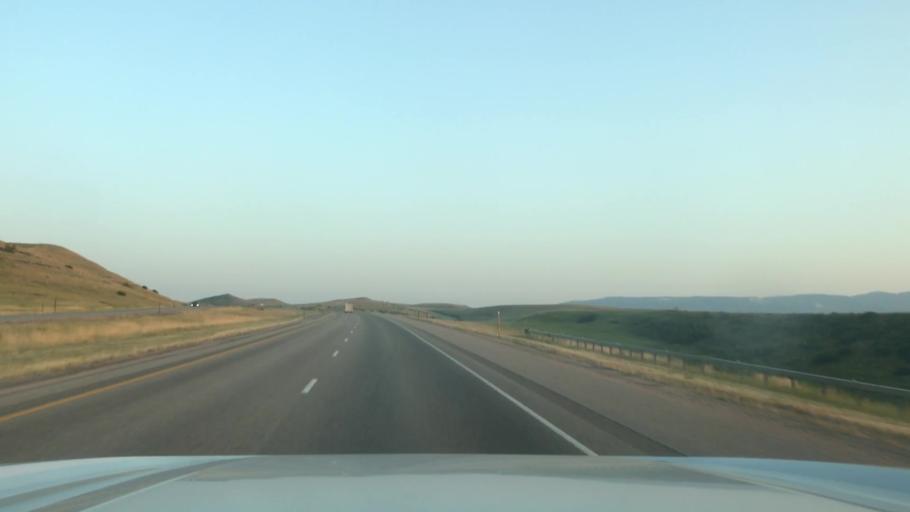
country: US
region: Wyoming
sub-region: Sheridan County
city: Sheridan
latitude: 44.7245
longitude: -106.9183
